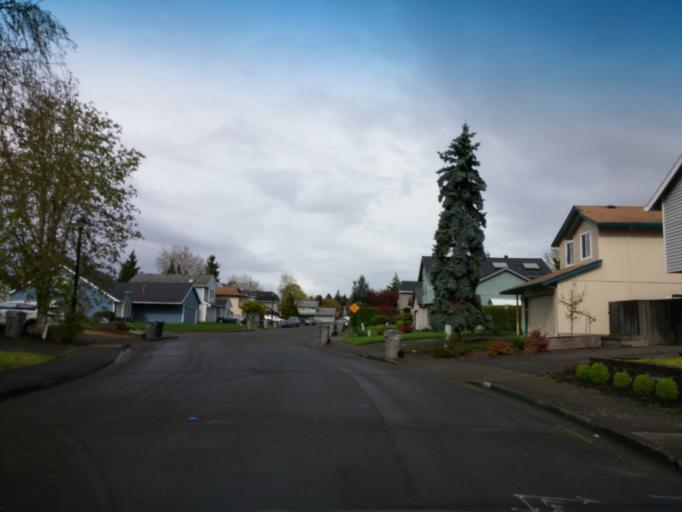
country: US
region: Oregon
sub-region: Washington County
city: Oak Hills
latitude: 45.5381
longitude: -122.8429
